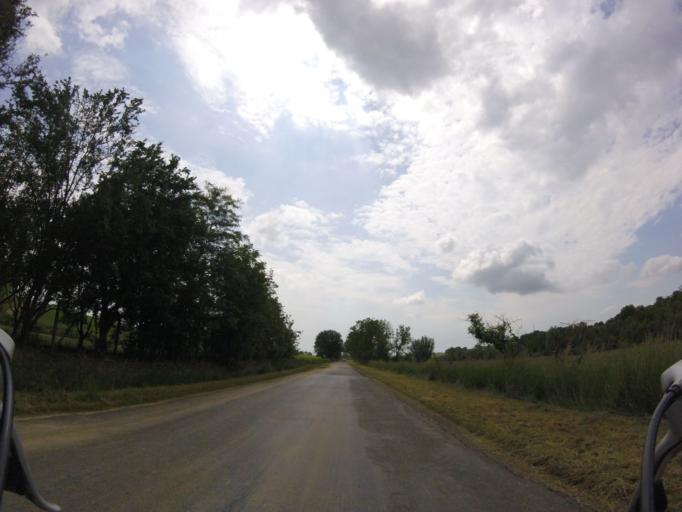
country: HU
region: Baranya
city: Kozarmisleny
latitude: 46.0546
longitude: 18.3776
